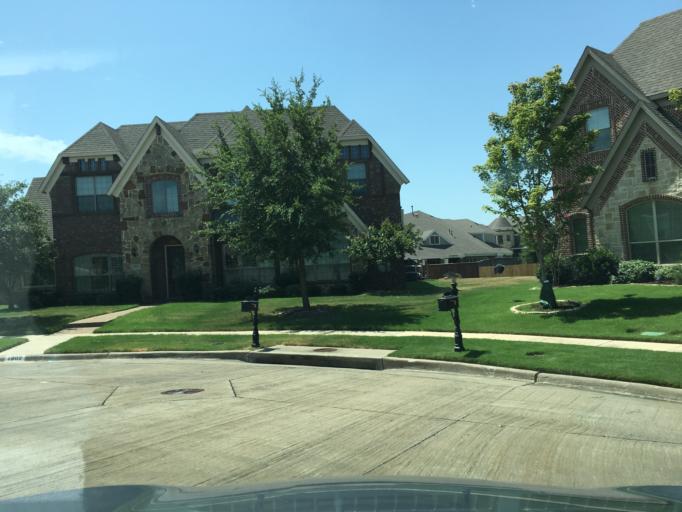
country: US
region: Texas
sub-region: Dallas County
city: Rowlett
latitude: 32.8877
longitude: -96.6018
